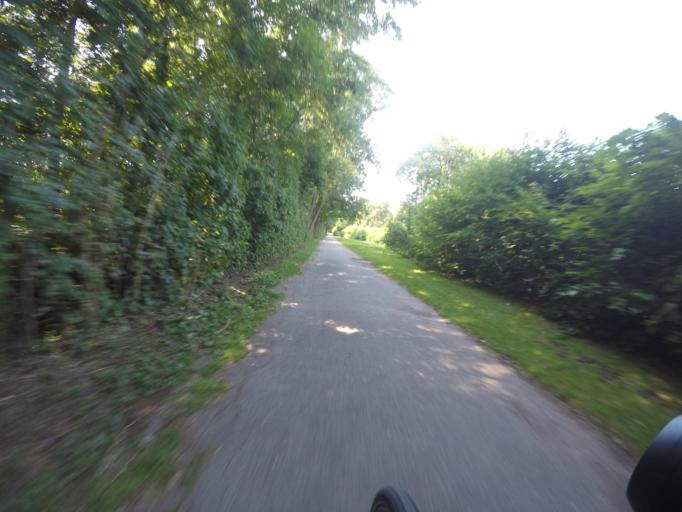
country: DE
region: Hamburg
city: Bergedorf
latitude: 53.5064
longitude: 10.2204
